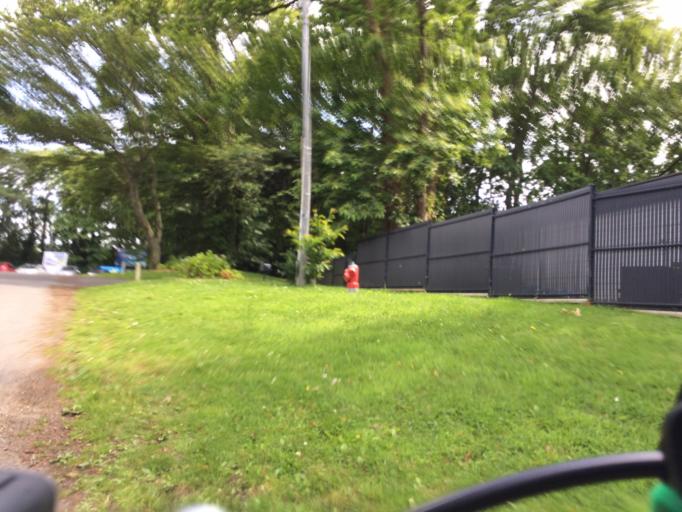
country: FR
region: Brittany
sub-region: Departement du Finistere
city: Logonna-Daoulas
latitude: 48.3187
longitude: -4.2852
